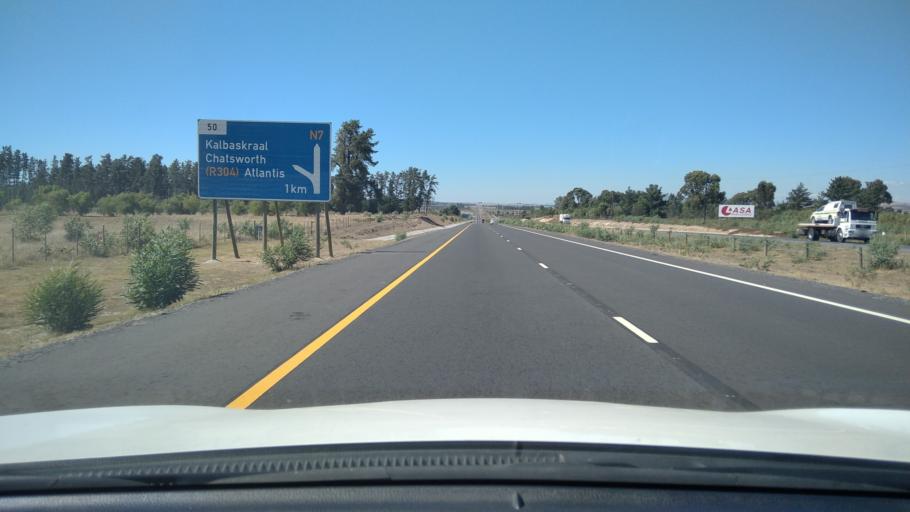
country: ZA
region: Western Cape
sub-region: City of Cape Town
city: Atlantis
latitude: -33.5925
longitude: 18.6057
